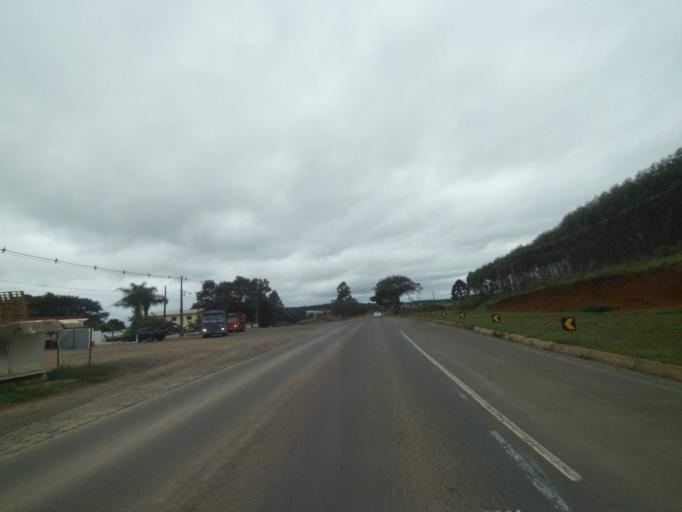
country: BR
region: Parana
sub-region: Telemaco Borba
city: Telemaco Borba
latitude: -24.3860
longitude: -50.6791
